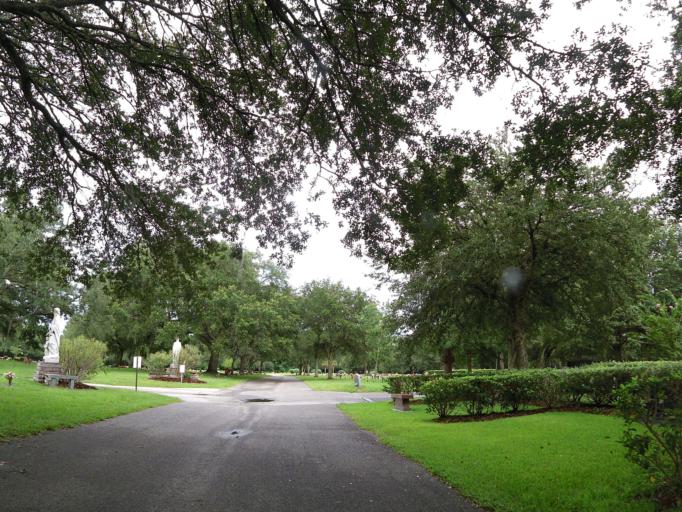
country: US
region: Florida
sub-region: Duval County
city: Jacksonville
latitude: 30.2954
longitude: -81.6226
